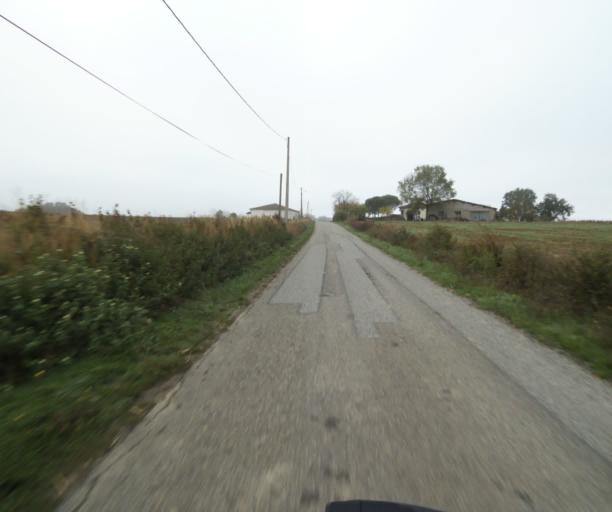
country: FR
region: Midi-Pyrenees
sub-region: Departement du Tarn-et-Garonne
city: Orgueil
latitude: 43.9293
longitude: 1.4380
